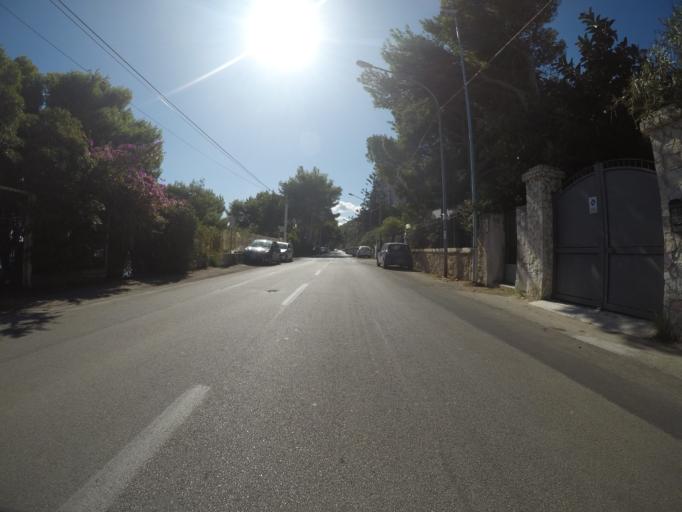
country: IT
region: Sicily
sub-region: Palermo
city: Palermo
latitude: 38.1904
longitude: 13.3586
